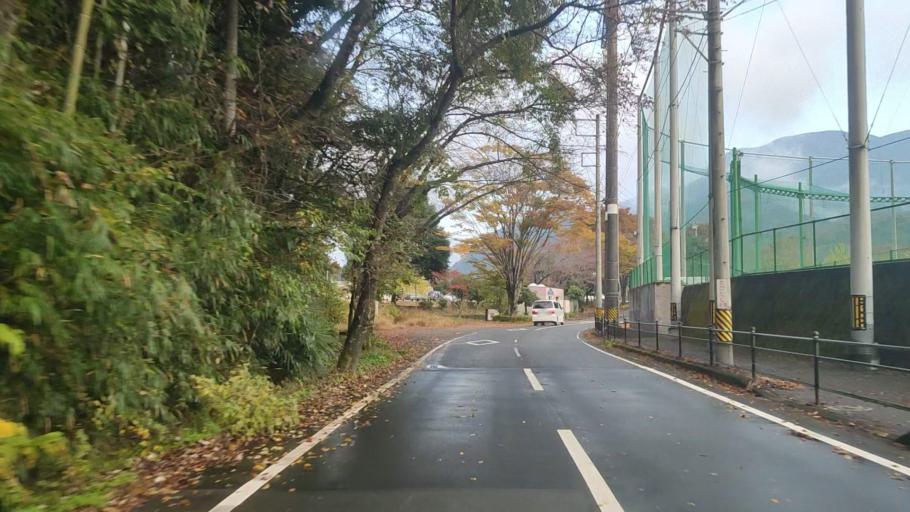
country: JP
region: Shizuoka
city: Fujinomiya
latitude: 35.2778
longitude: 138.4570
